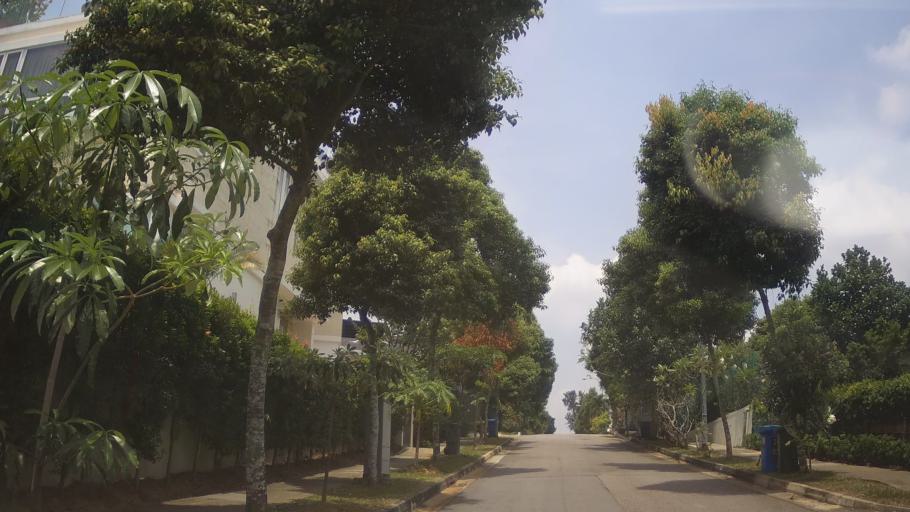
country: MY
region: Johor
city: Johor Bahru
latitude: 1.3707
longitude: 103.7725
